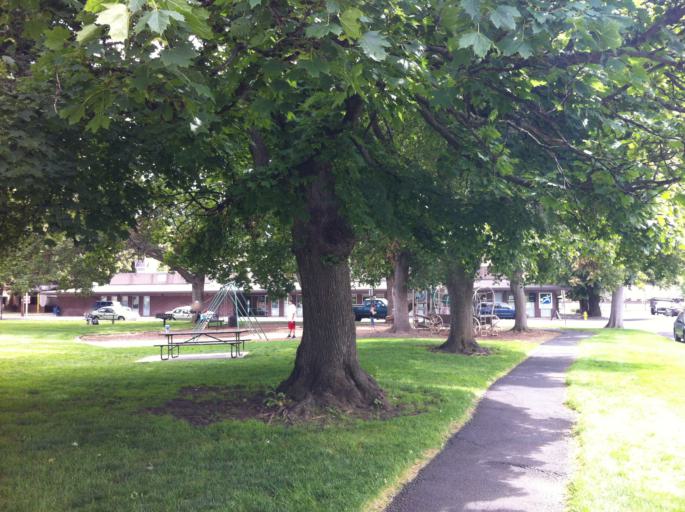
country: US
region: Oregon
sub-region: Umatilla County
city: Pendleton
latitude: 45.6732
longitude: -118.7800
